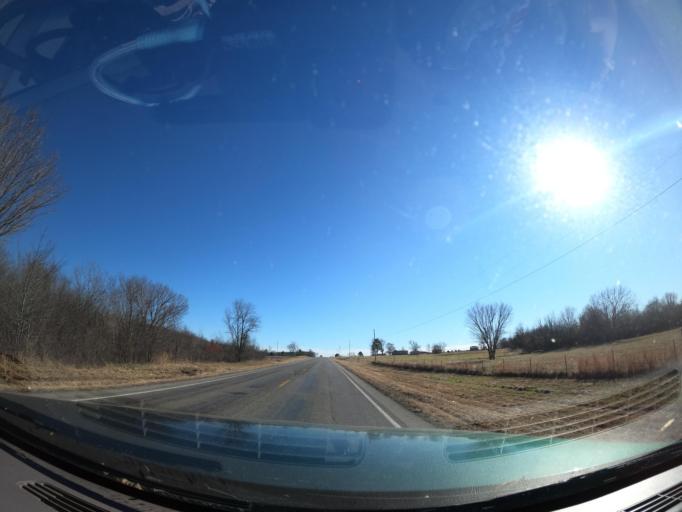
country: US
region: Oklahoma
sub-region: Muskogee County
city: Haskell
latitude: 35.7666
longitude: -95.6509
